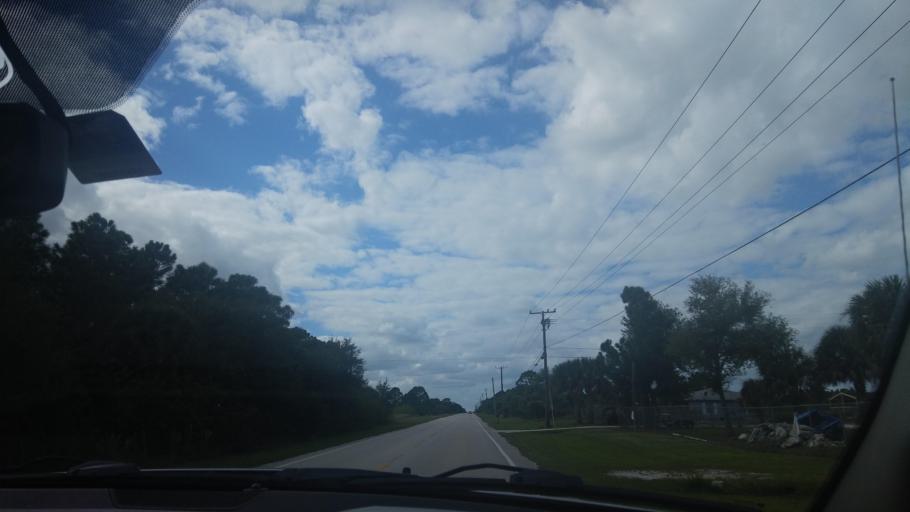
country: US
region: Florida
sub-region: Indian River County
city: Winter Beach
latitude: 27.7338
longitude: -80.4321
